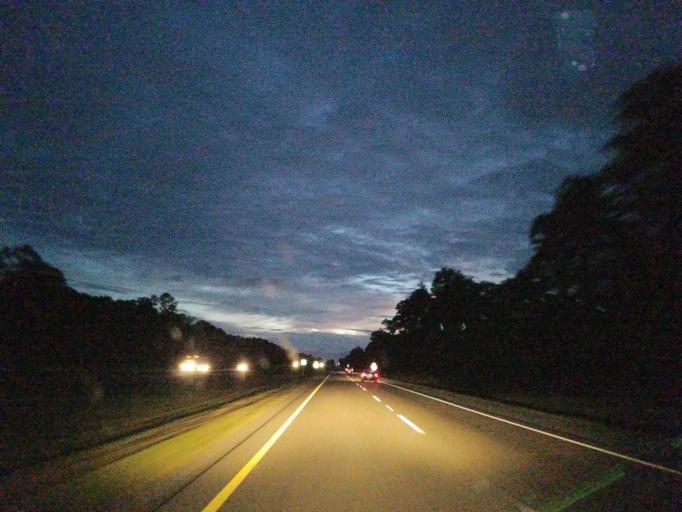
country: US
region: Mississippi
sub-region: Jones County
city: Sharon
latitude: 31.7542
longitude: -89.0710
